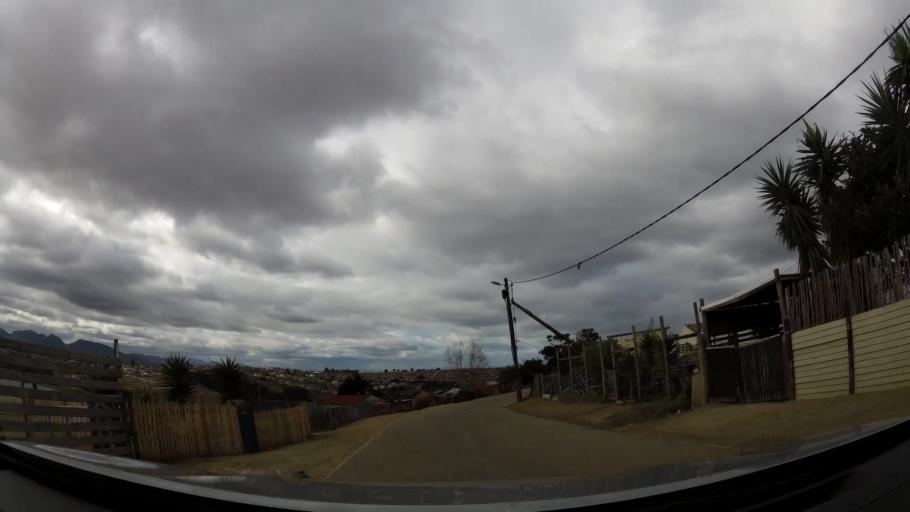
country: ZA
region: Western Cape
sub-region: Eden District Municipality
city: George
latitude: -34.0190
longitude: 22.4823
